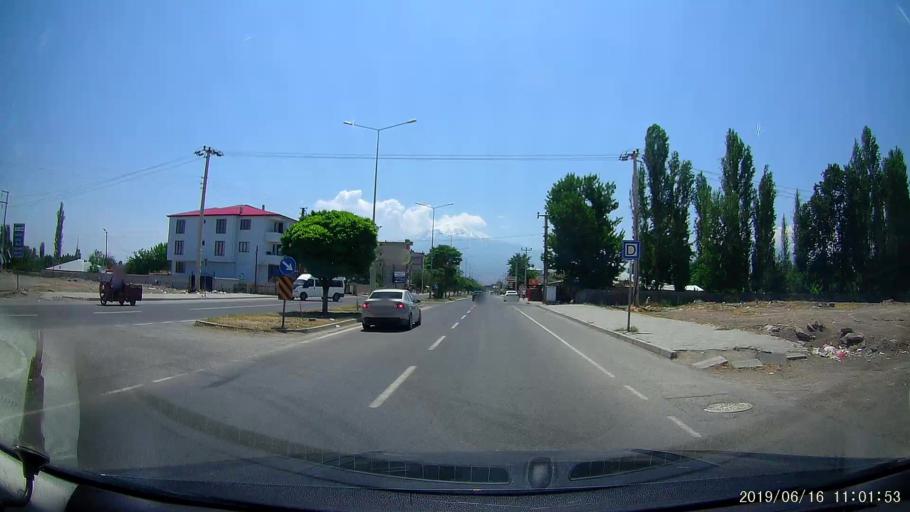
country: TR
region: Igdir
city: Igdir
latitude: 39.9116
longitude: 44.0545
